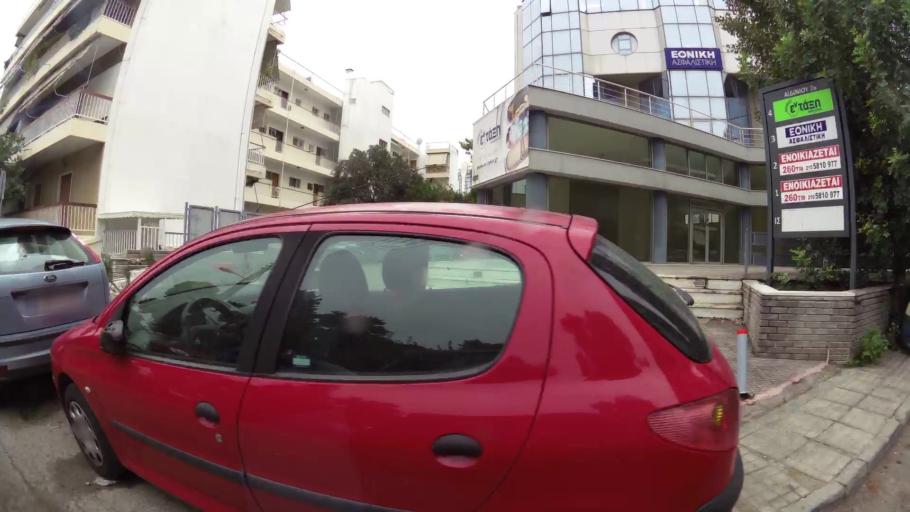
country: GR
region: Attica
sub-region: Nomarchia Athinas
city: Chaidari
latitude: 38.0110
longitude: 23.6652
